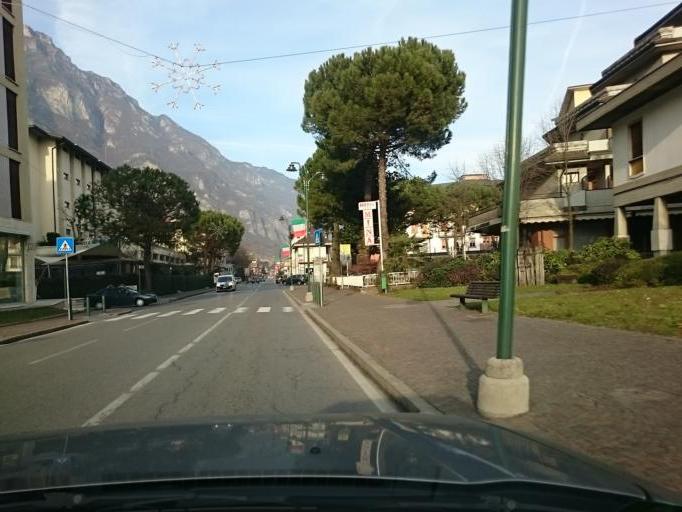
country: IT
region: Lombardy
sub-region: Provincia di Brescia
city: Darfo Boario Terme
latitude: 45.8922
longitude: 10.1881
